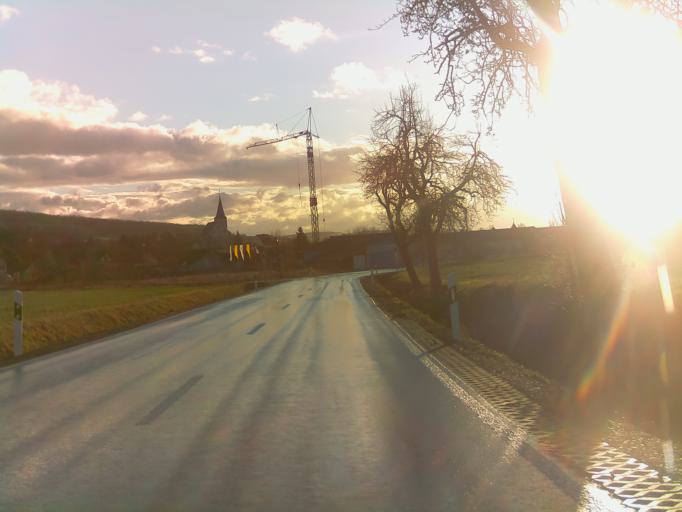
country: DE
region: Bavaria
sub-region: Regierungsbezirk Unterfranken
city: Sondheim vor der Rhoen
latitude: 50.4822
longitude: 10.1754
